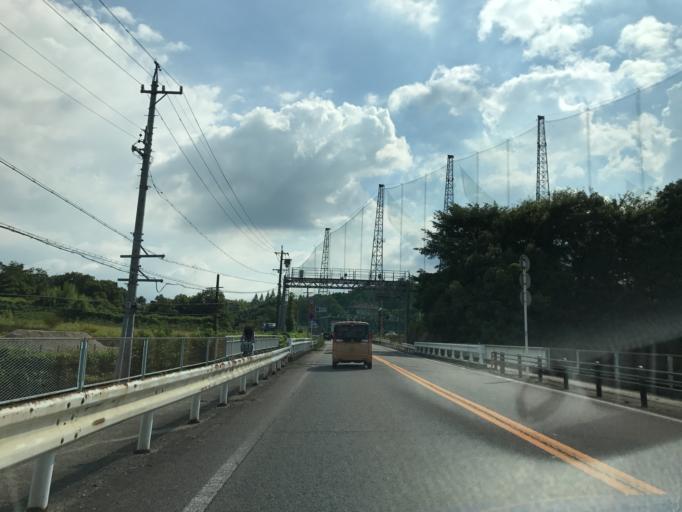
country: JP
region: Gifu
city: Kakamigahara
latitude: 35.4664
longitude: 136.8573
